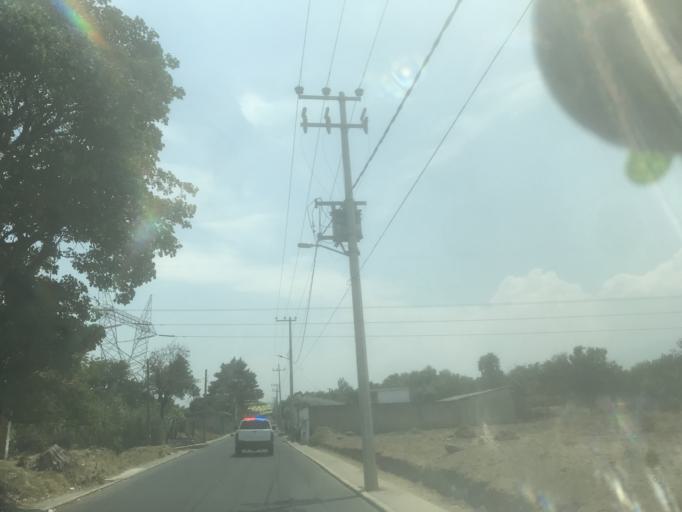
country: MX
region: Mexico
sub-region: Ozumba
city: San Jose Tlacotitlan
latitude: 18.9847
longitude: -98.8077
